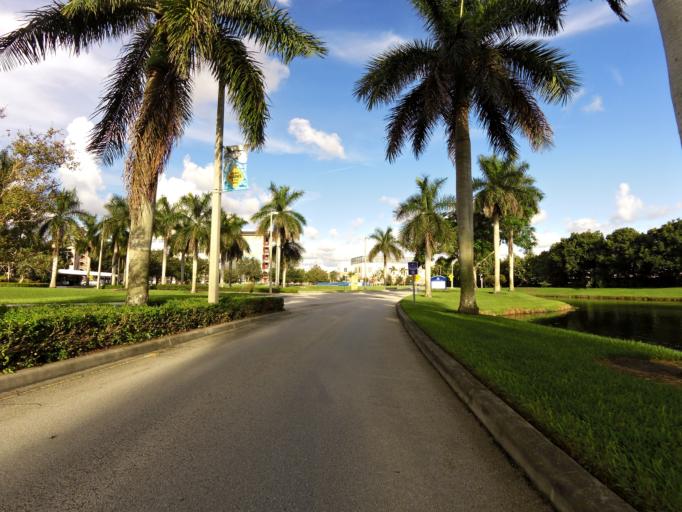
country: US
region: Florida
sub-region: Broward County
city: Davie
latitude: 26.0806
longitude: -80.2504
